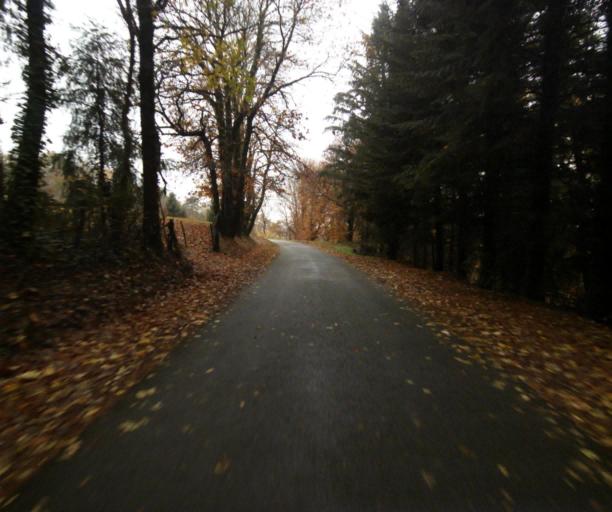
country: FR
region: Limousin
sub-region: Departement de la Correze
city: Cornil
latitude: 45.1966
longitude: 1.6423
